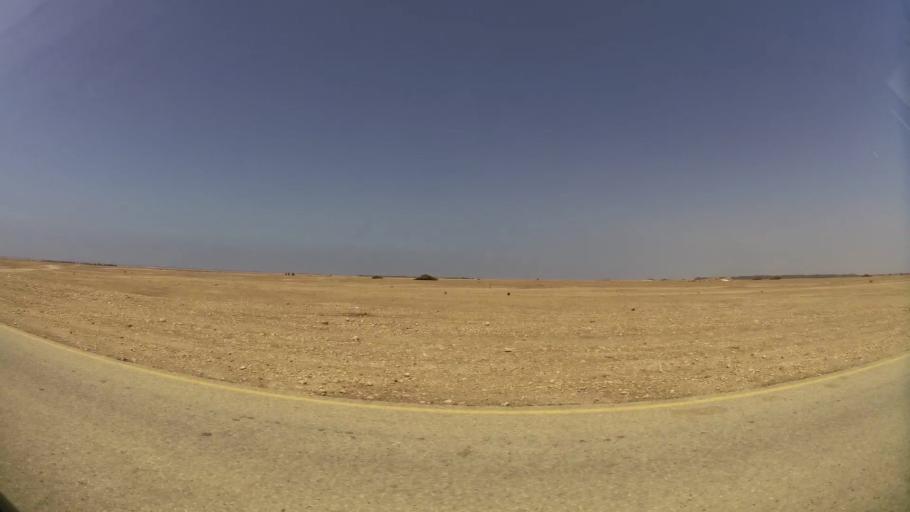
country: OM
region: Zufar
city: Salalah
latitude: 17.0409
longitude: 54.2489
